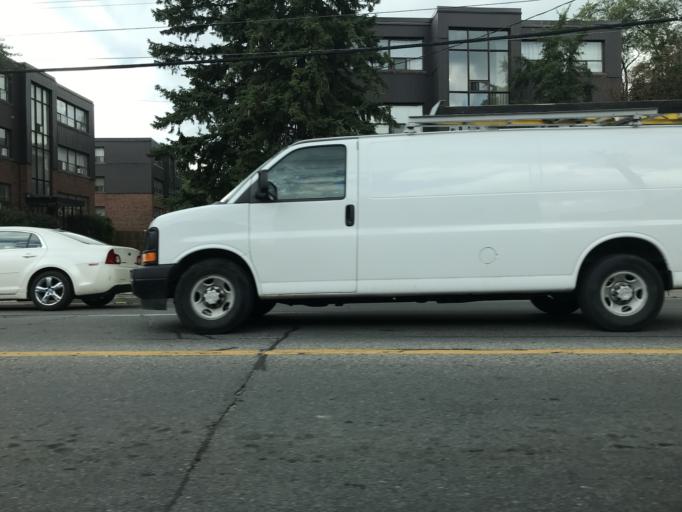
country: CA
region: Ontario
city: Toronto
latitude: 43.7238
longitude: -79.4308
